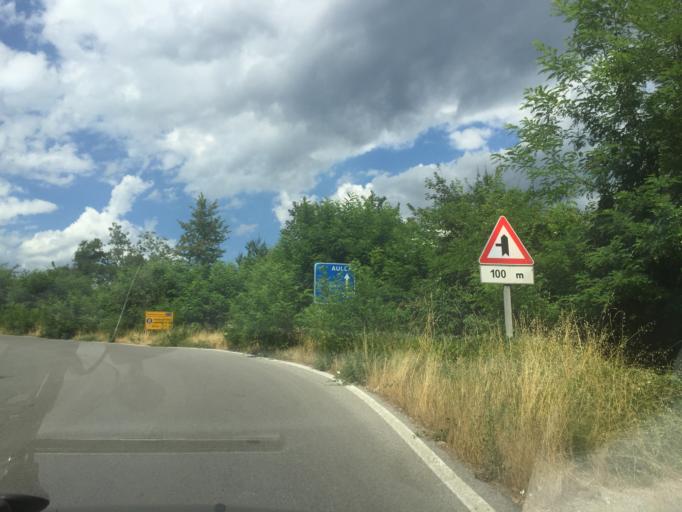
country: IT
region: Tuscany
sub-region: Provincia di Lucca
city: Castelnuovo di Garfagnana
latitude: 44.1180
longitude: 10.3947
